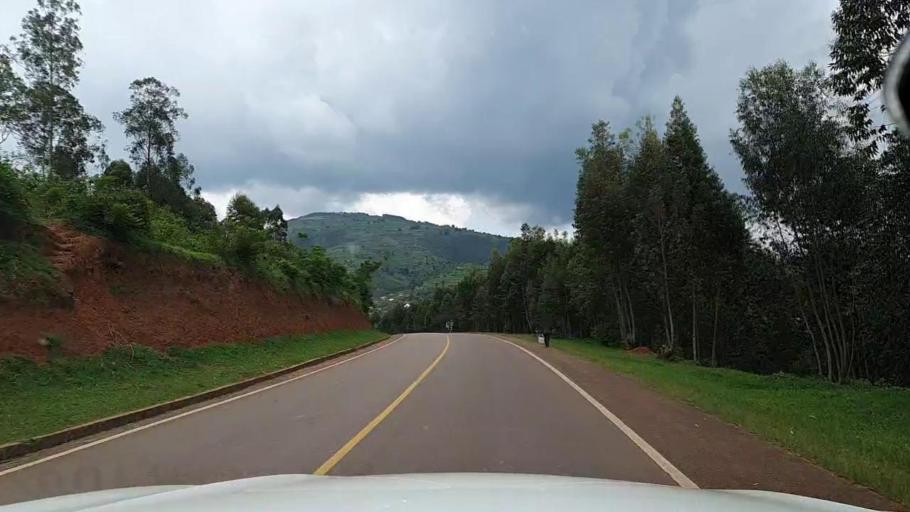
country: RW
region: Kigali
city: Kigali
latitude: -1.7740
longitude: 30.1265
